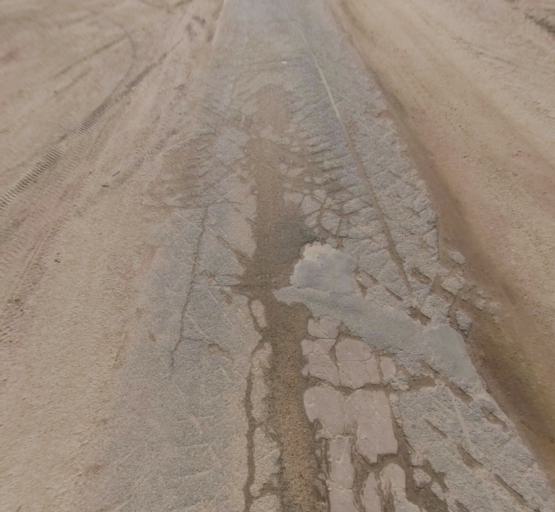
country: US
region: California
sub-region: Madera County
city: Chowchilla
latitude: 37.1419
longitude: -120.2665
